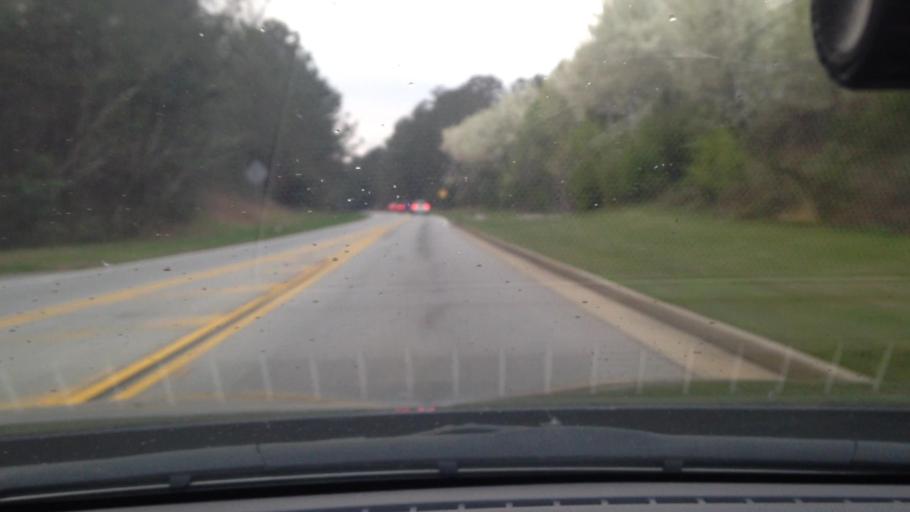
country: US
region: Georgia
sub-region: Coweta County
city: East Newnan
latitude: 33.3773
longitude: -84.7175
